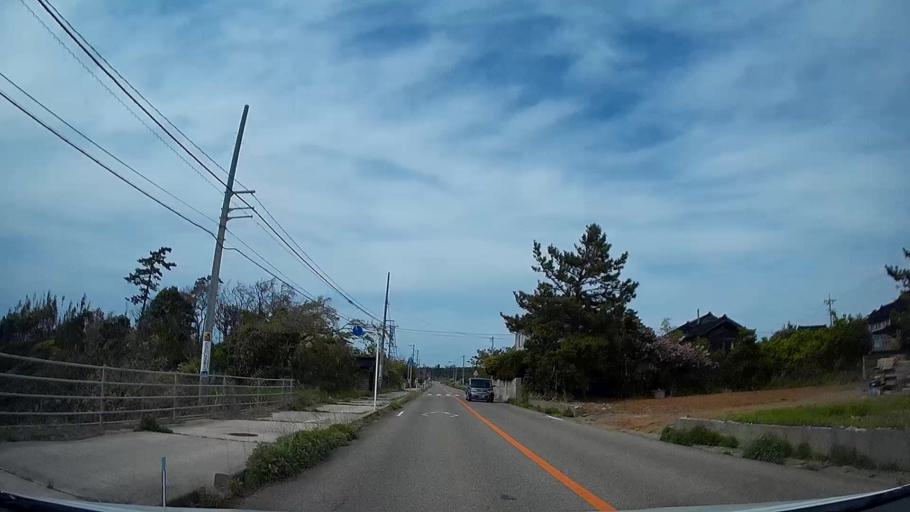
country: JP
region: Ishikawa
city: Hakui
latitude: 37.0286
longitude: 136.7474
